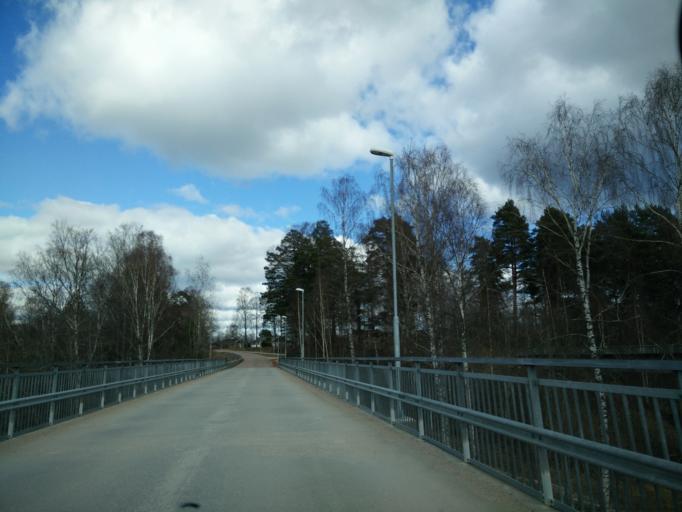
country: SE
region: Vaermland
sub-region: Hagfors Kommun
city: Hagfors
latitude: 60.0011
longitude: 13.5969
